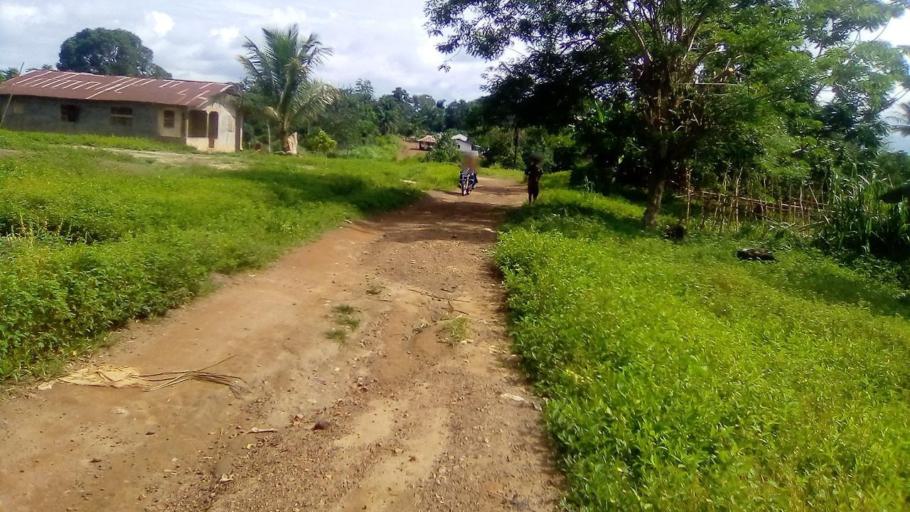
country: SL
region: Southern Province
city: Pujehun
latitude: 7.3718
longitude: -11.7276
